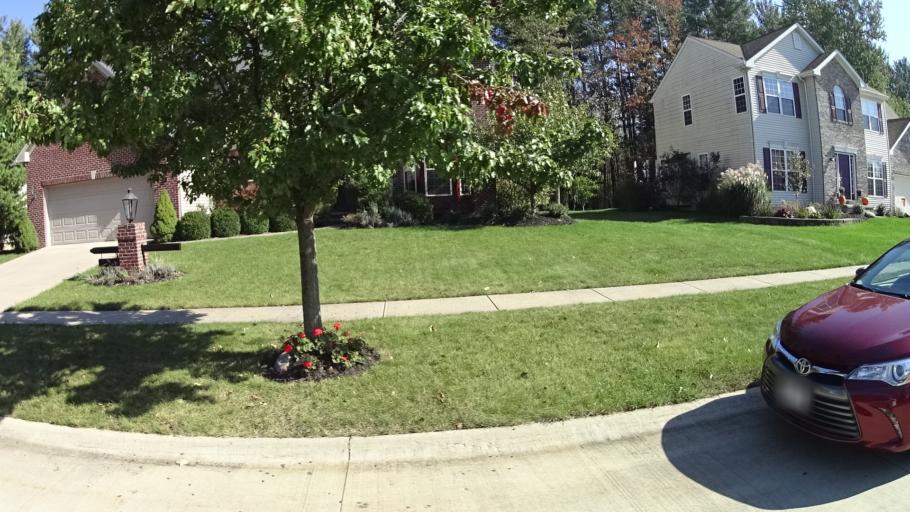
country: US
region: Ohio
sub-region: Lorain County
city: Vermilion-on-the-Lake
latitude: 41.4159
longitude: -82.3369
